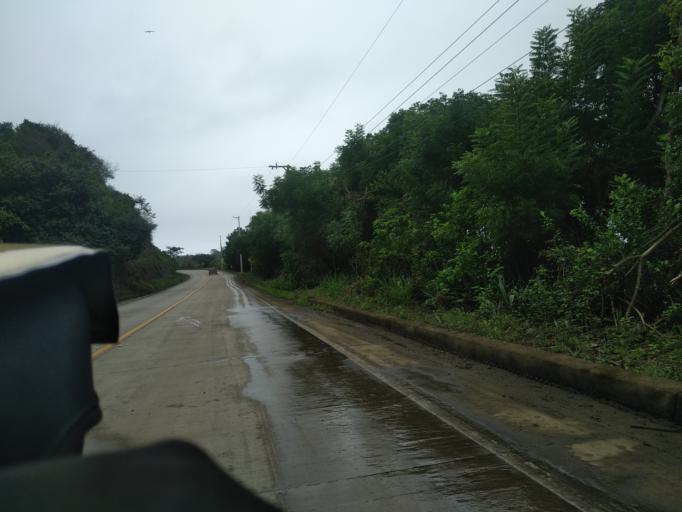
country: EC
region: Manabi
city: Pajan
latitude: -1.6790
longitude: -80.8103
